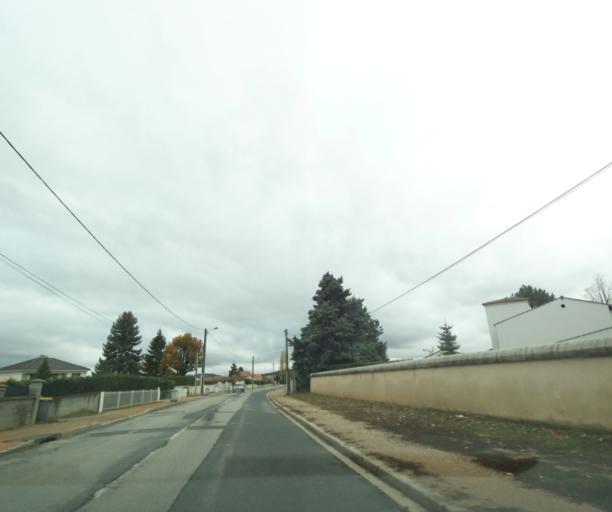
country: FR
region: Auvergne
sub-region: Departement du Puy-de-Dome
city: Pont-du-Chateau
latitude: 45.8088
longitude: 3.2426
